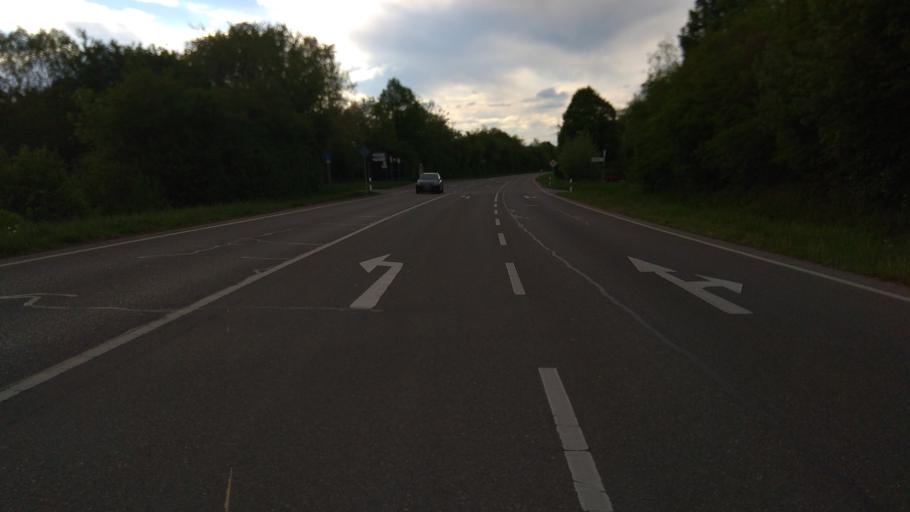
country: DE
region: Baden-Wuerttemberg
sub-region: Tuebingen Region
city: Wannweil
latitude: 48.5029
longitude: 9.1691
